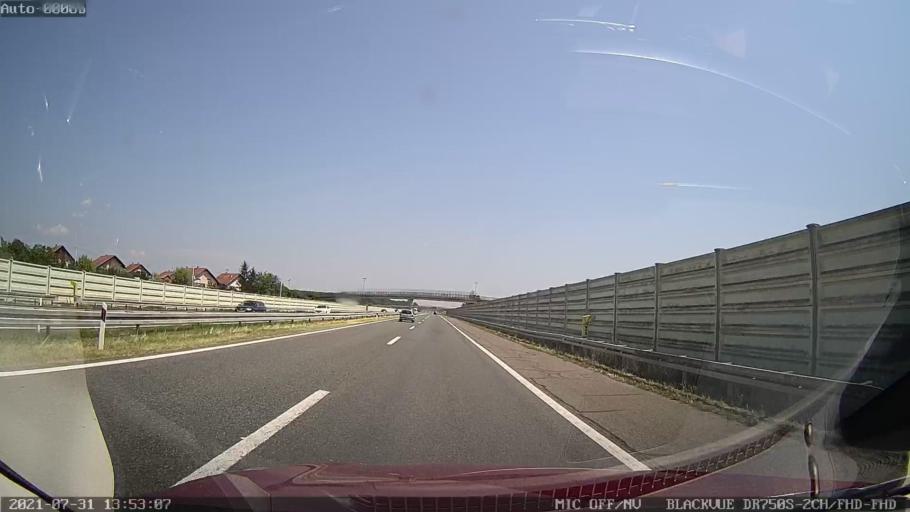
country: HR
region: Brodsko-Posavska
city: Bukovlje
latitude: 45.1798
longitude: 18.0580
